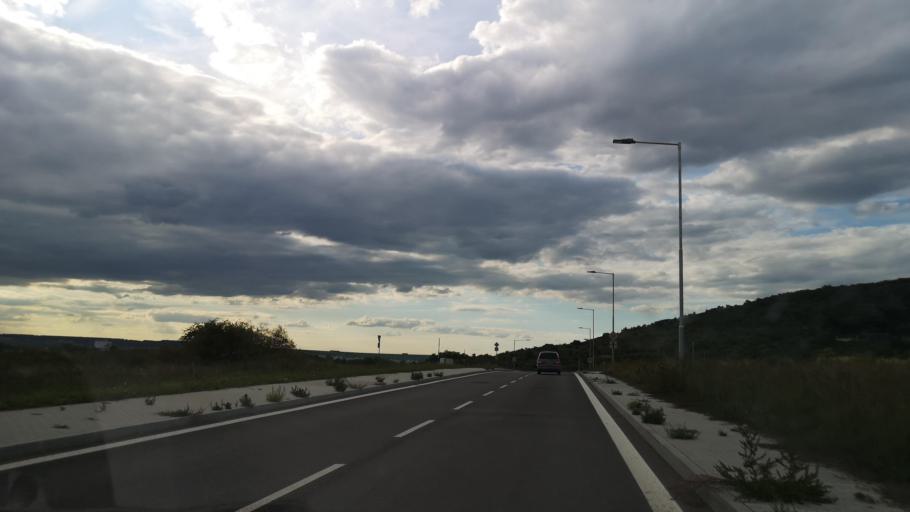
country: SK
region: Nitriansky
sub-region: Okres Nitra
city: Nitra
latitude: 48.3327
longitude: 18.0819
